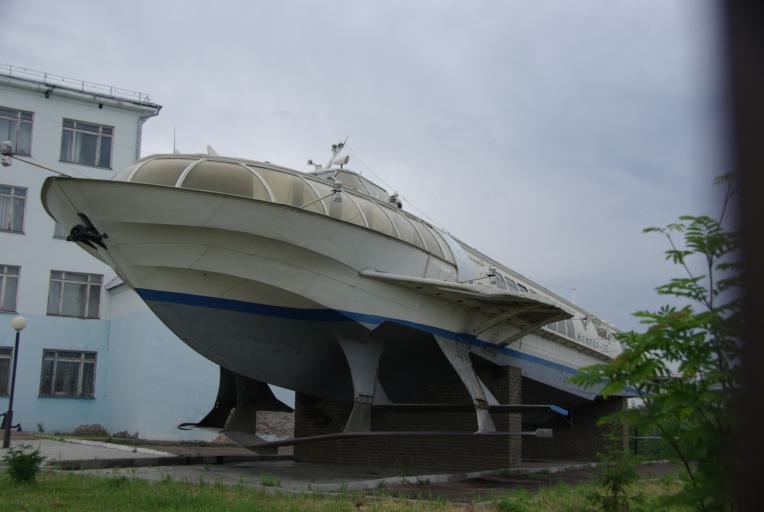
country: RU
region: Tatarstan
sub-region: Gorod Kazan'
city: Kazan
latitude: 55.8040
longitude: 49.0752
